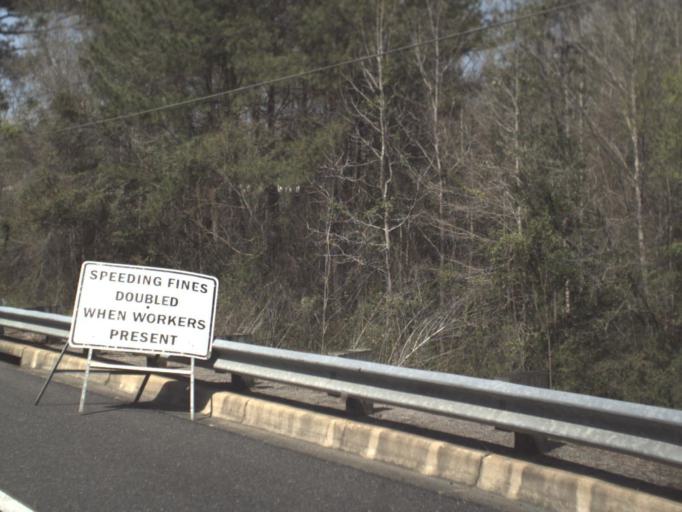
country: US
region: Florida
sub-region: Gadsden County
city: Quincy
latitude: 30.5647
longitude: -84.5418
